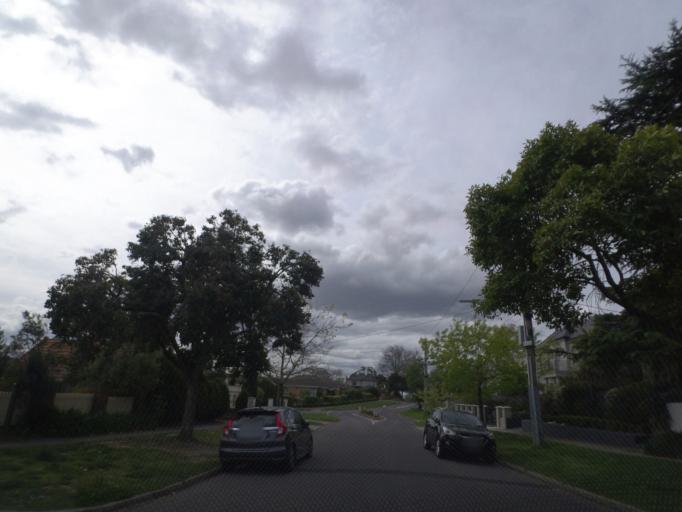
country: AU
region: Victoria
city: Mont Albert
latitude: -37.8078
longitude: 145.0962
